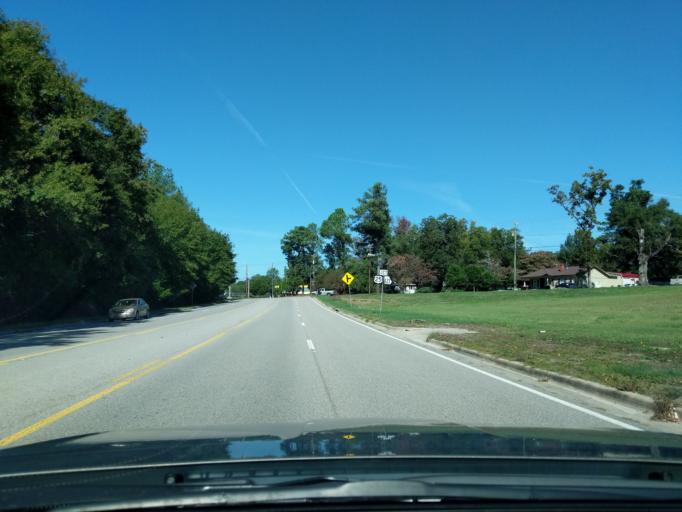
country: US
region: Georgia
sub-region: Richmond County
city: Augusta
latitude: 33.4330
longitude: -82.0085
